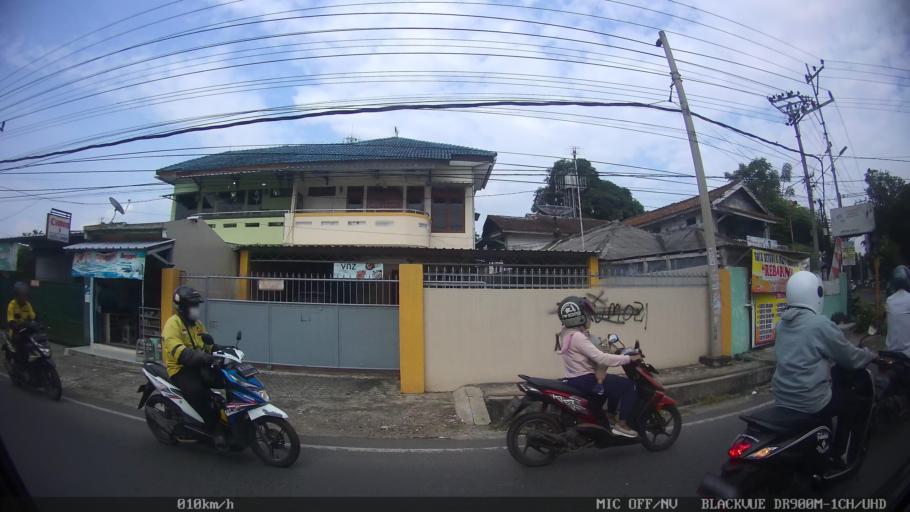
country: ID
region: Lampung
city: Bandarlampung
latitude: -5.4361
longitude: 105.2518
